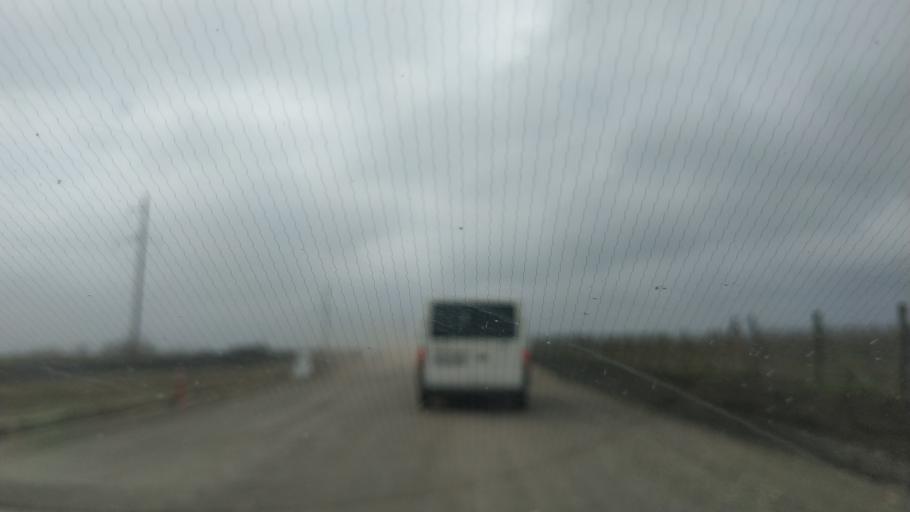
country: MD
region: Gagauzia
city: Bugeac
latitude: 46.3254
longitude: 28.7284
